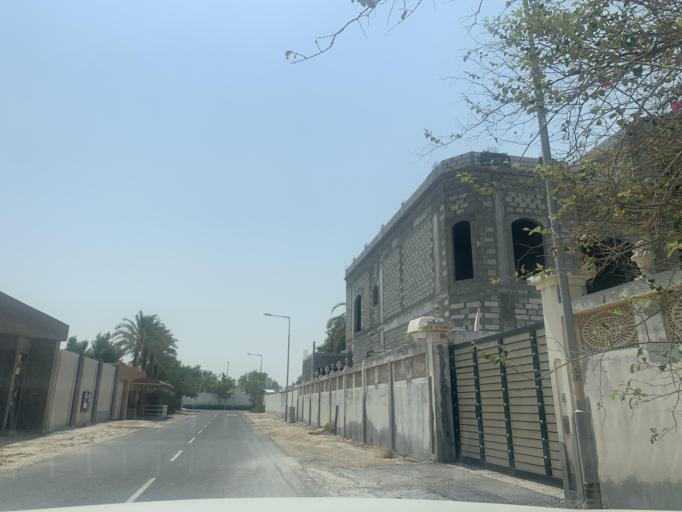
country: BH
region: Central Governorate
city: Madinat Hamad
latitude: 26.1466
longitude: 50.4741
